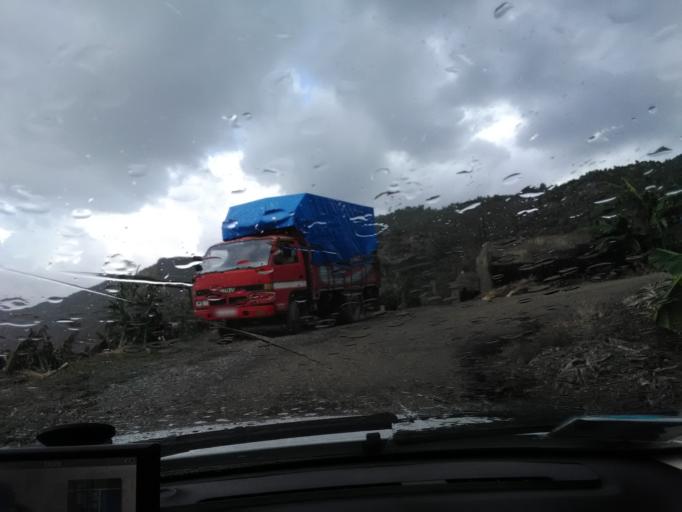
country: TR
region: Antalya
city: Gazipasa
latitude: 36.1591
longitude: 32.4199
